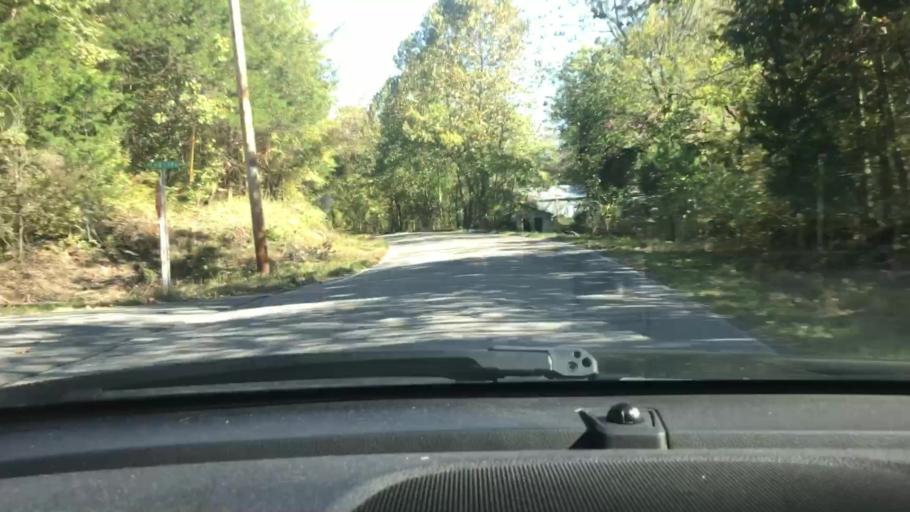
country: US
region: Tennessee
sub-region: Dickson County
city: Charlotte
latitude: 36.1792
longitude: -87.2797
